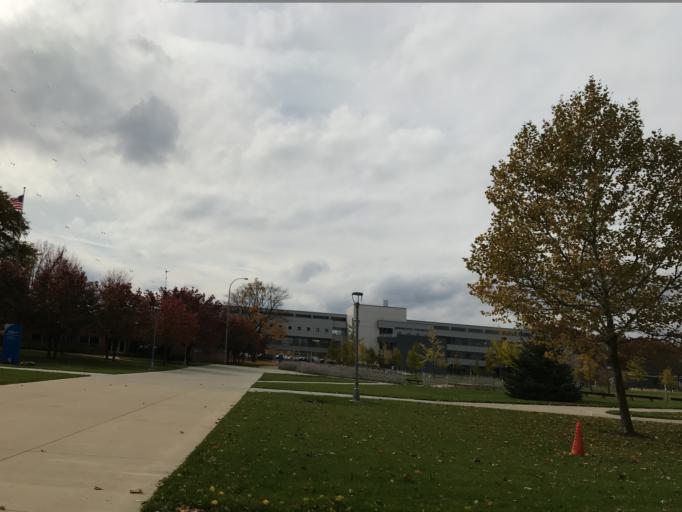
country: US
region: Michigan
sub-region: Oakland County
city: Southfield
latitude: 42.4750
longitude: -83.2483
